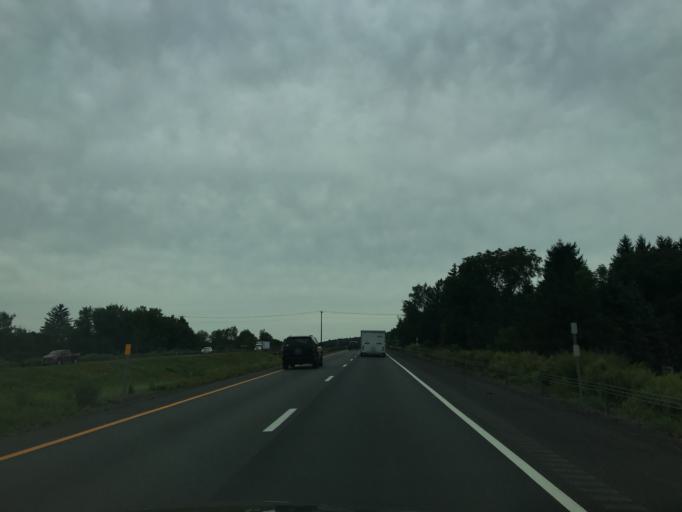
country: US
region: Pennsylvania
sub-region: Susquehanna County
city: Hallstead
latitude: 42.0654
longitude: -75.7982
